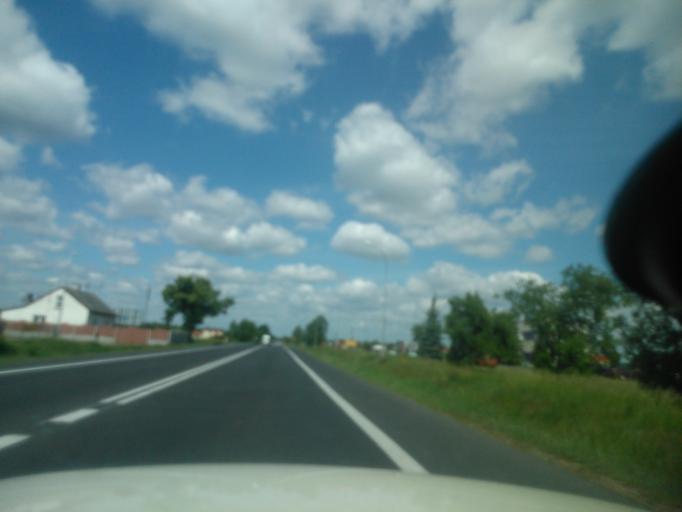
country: PL
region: Kujawsko-Pomorskie
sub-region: Powiat torunski
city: Lubicz Gorny
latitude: 53.0156
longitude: 18.8162
